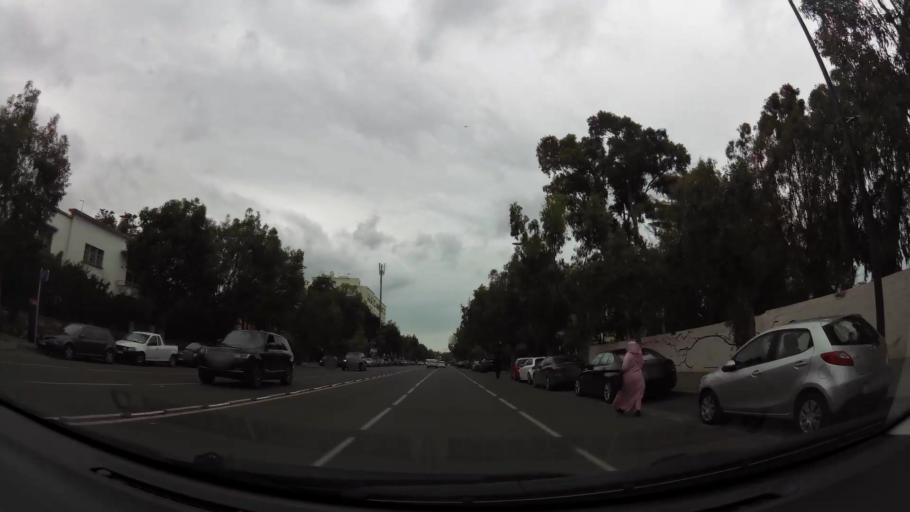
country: MA
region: Grand Casablanca
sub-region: Casablanca
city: Casablanca
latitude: 33.5886
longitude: -7.6462
